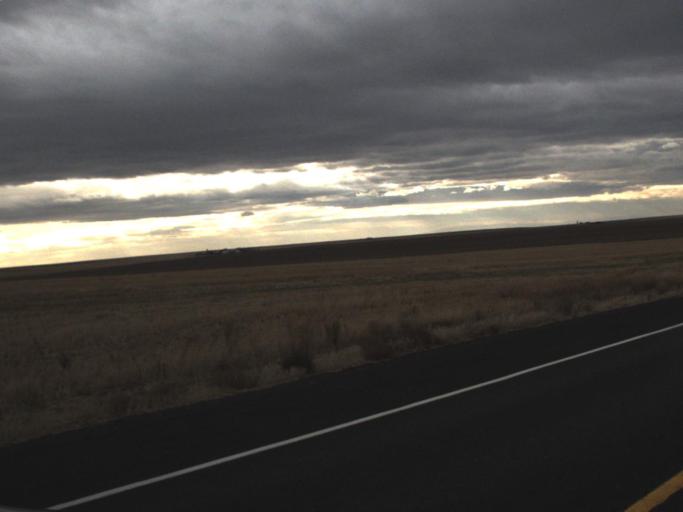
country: US
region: Washington
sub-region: Franklin County
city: Connell
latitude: 46.7945
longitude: -118.6215
